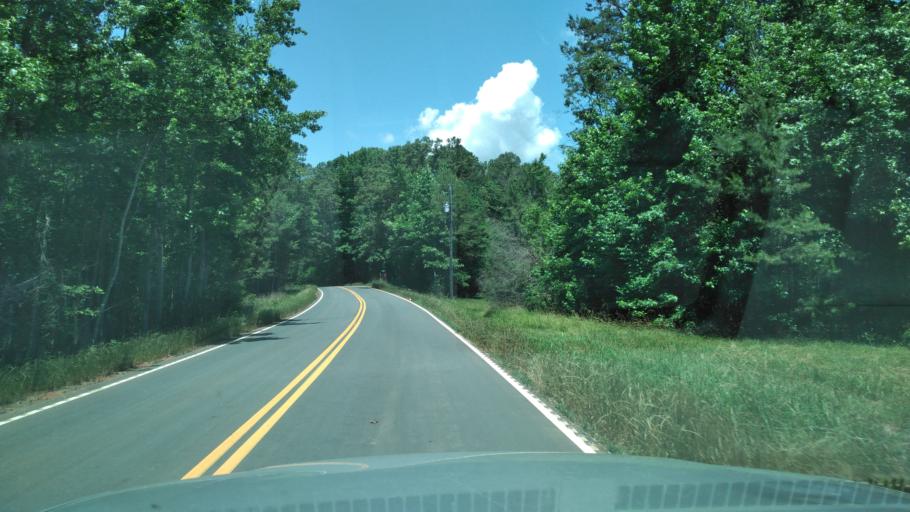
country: US
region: South Carolina
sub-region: Greenwood County
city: Ware Shoals
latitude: 34.4203
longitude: -82.1317
